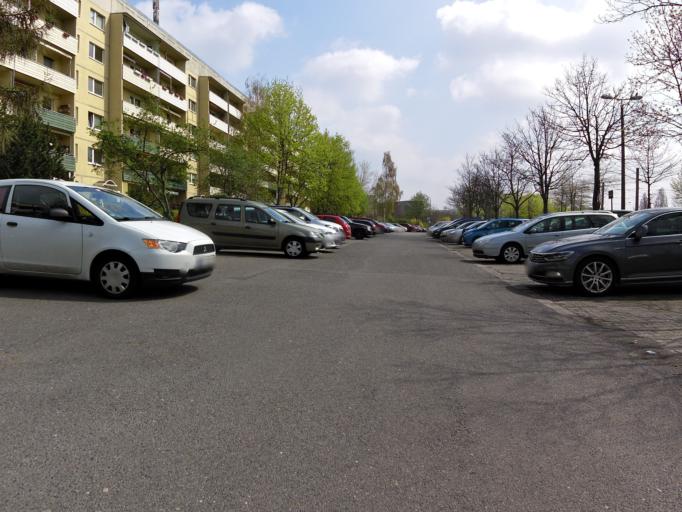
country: DE
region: Saxony
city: Markranstadt
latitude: 51.3235
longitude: 12.2656
